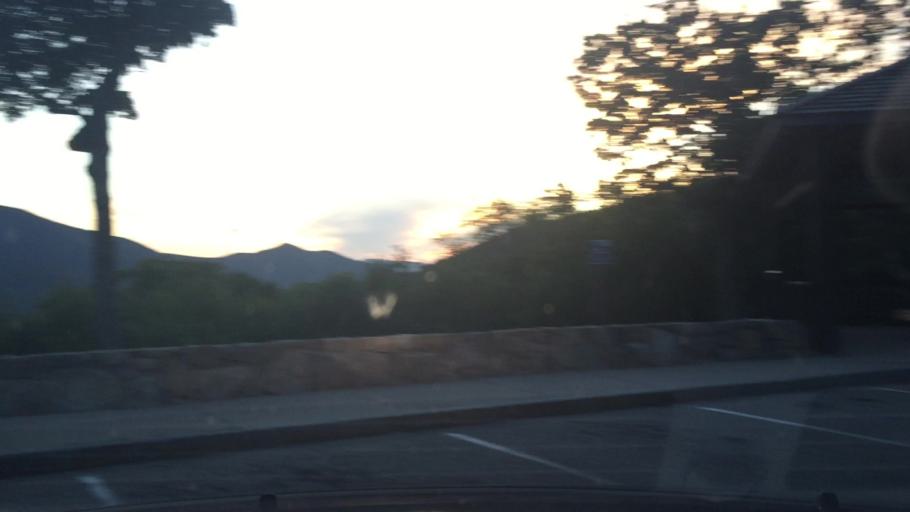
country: US
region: New Hampshire
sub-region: Grafton County
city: Woodstock
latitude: 44.0407
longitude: -71.5234
